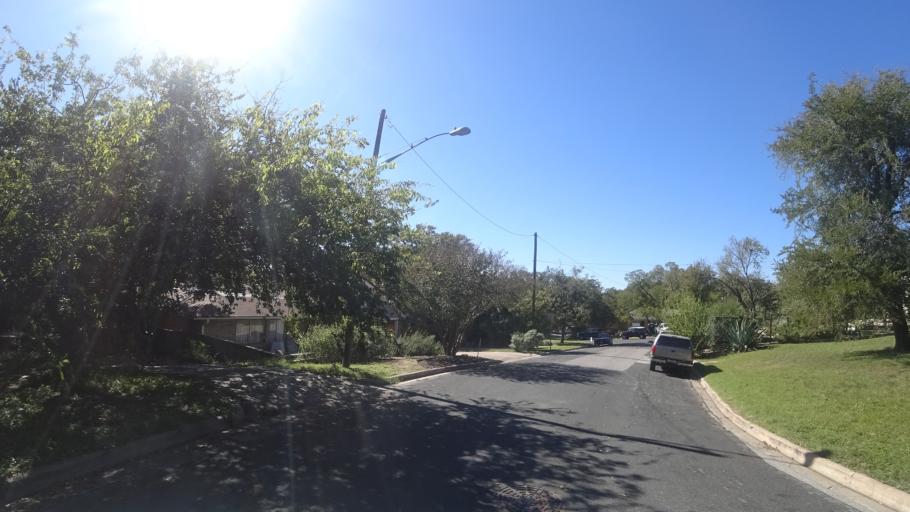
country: US
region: Texas
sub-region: Travis County
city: Austin
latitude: 30.2742
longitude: -97.7584
